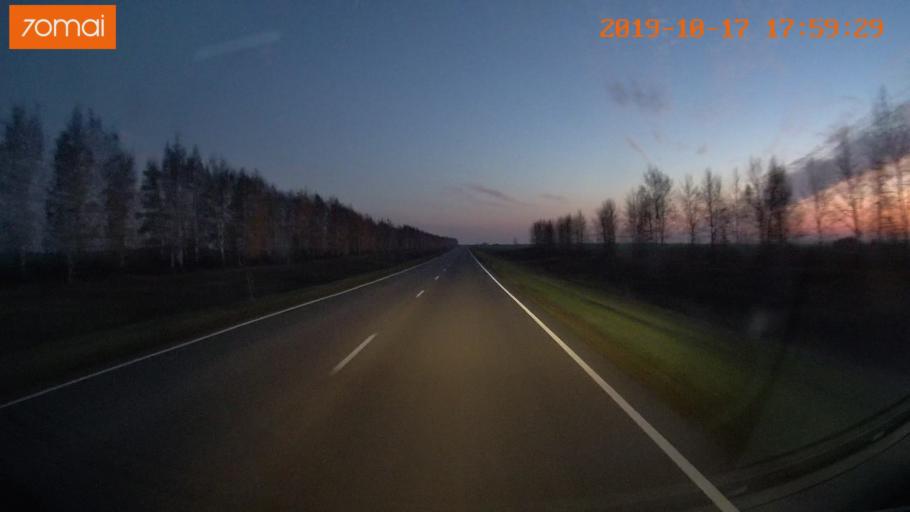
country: RU
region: Tula
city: Kurkino
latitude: 53.5376
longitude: 38.6211
